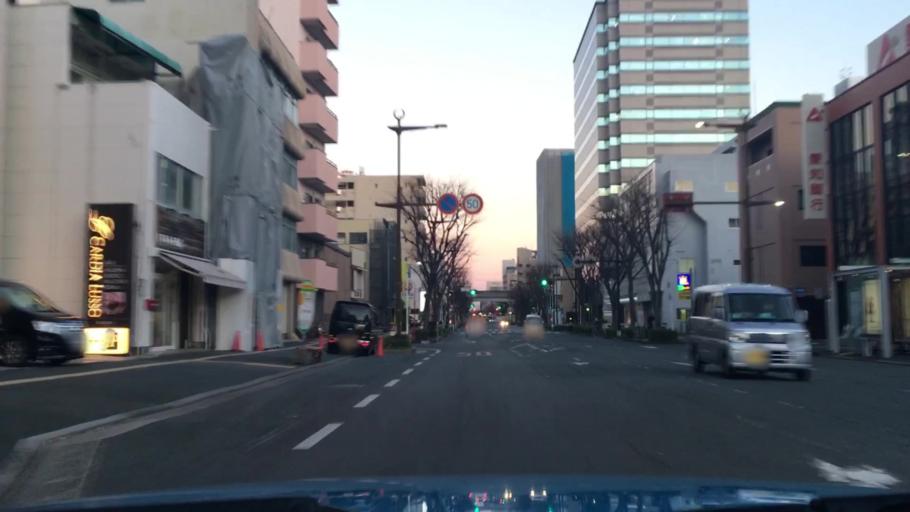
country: JP
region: Shizuoka
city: Hamamatsu
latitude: 34.7102
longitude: 137.7298
